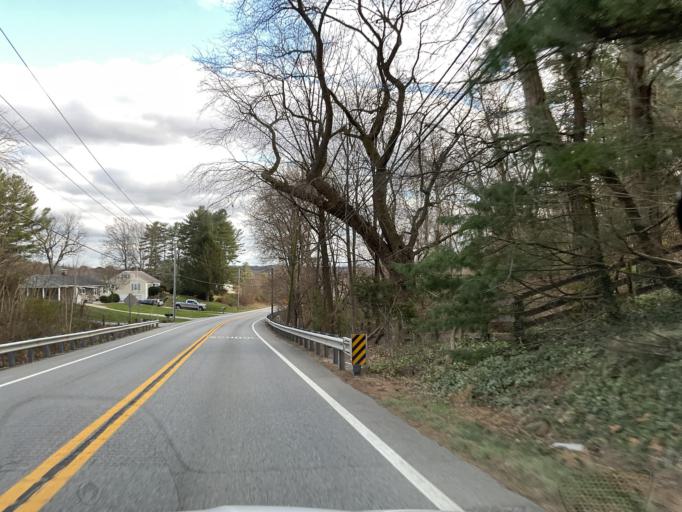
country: US
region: Pennsylvania
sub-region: Adams County
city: Mount Pleasant
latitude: 39.6784
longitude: -77.0381
